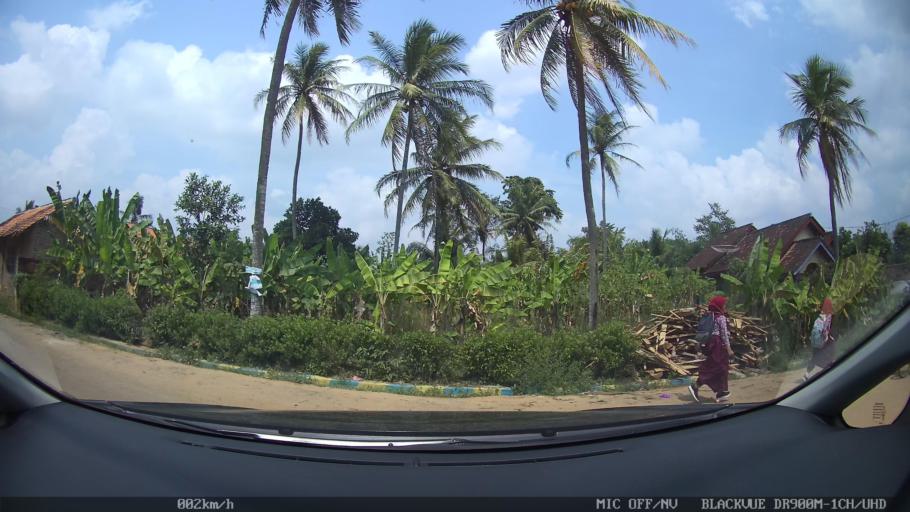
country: ID
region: Lampung
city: Pringsewu
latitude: -5.3856
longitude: 104.9604
